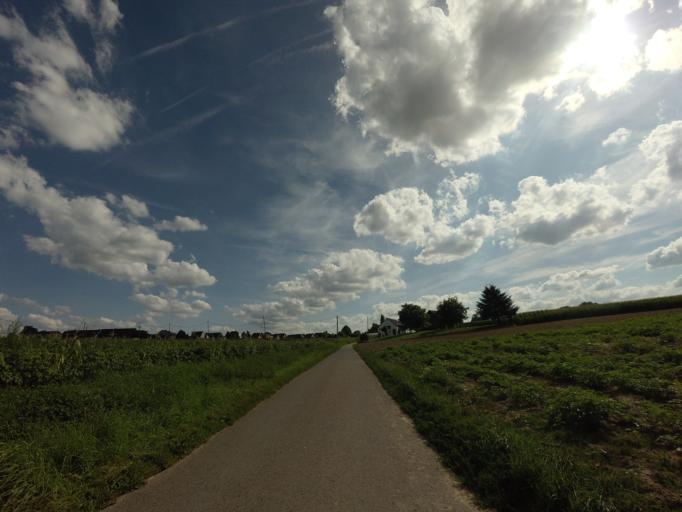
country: BE
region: Flanders
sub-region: Provincie Vlaams-Brabant
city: Meise
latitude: 50.9481
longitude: 4.3387
